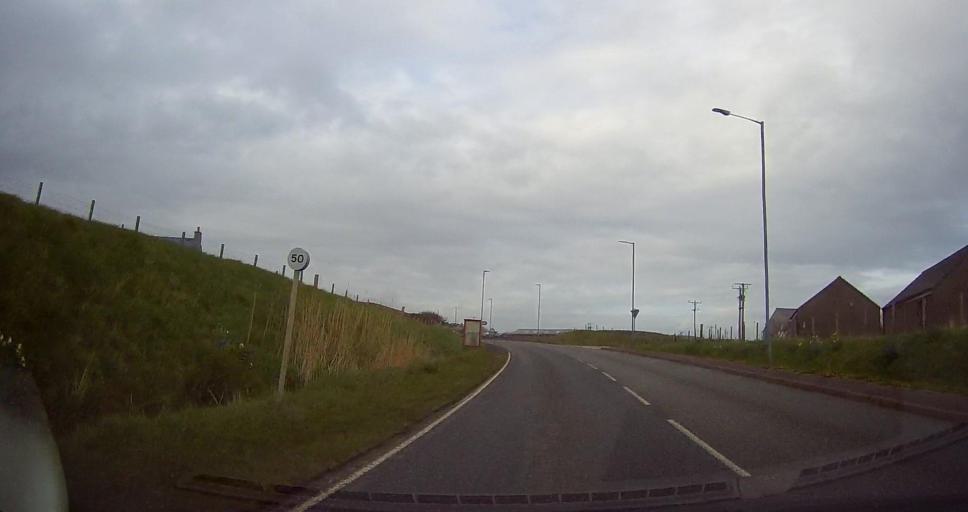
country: GB
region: Scotland
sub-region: Shetland Islands
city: Sandwick
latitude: 60.0378
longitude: -1.2297
